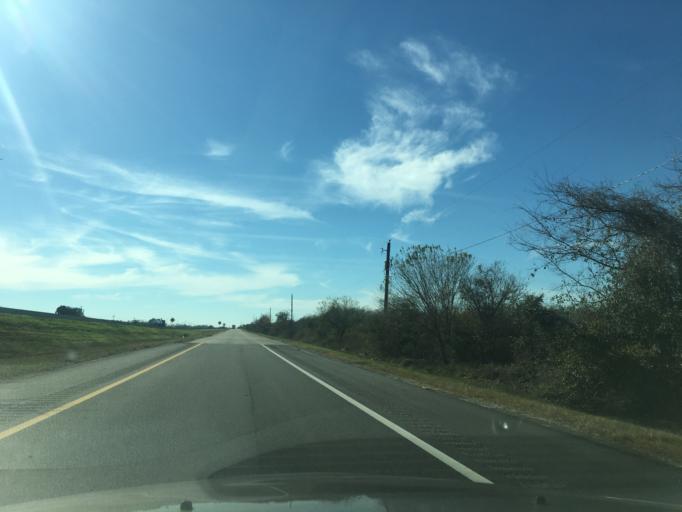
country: US
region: Texas
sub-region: Fort Bend County
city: Pleak
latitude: 29.4842
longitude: -95.9395
